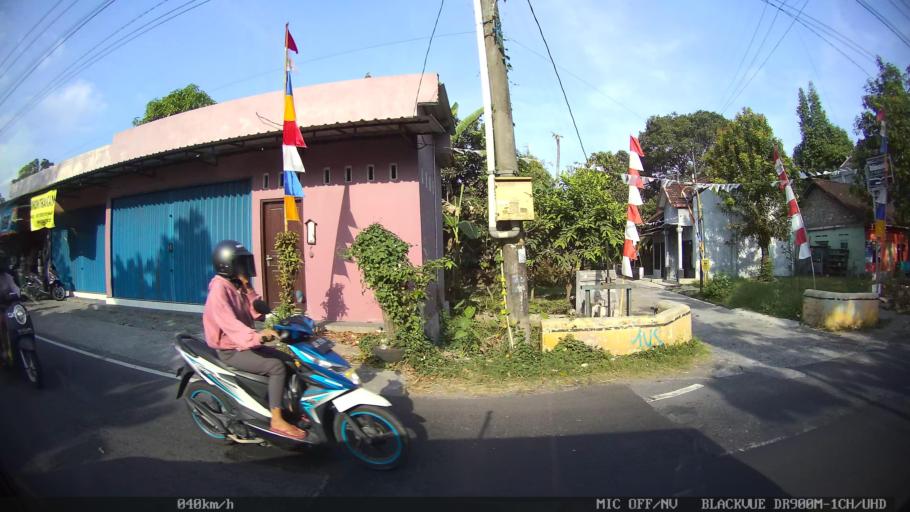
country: ID
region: Daerah Istimewa Yogyakarta
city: Bantul
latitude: -7.8889
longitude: 110.3174
